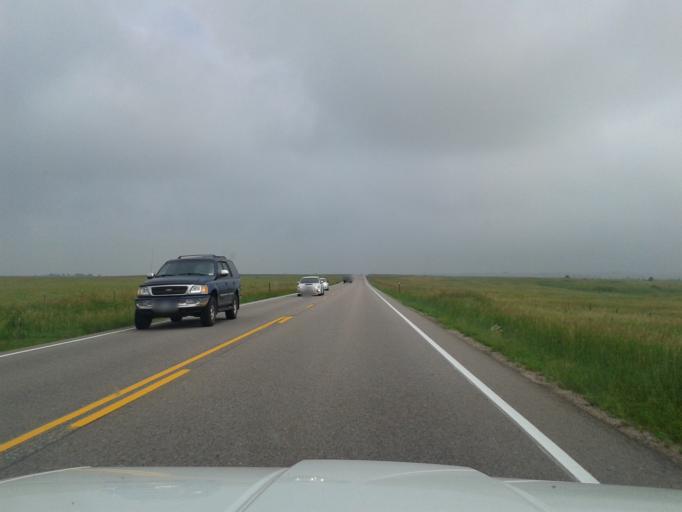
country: US
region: Colorado
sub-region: Elbert County
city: Ponderosa Park
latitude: 39.3059
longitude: -104.7355
